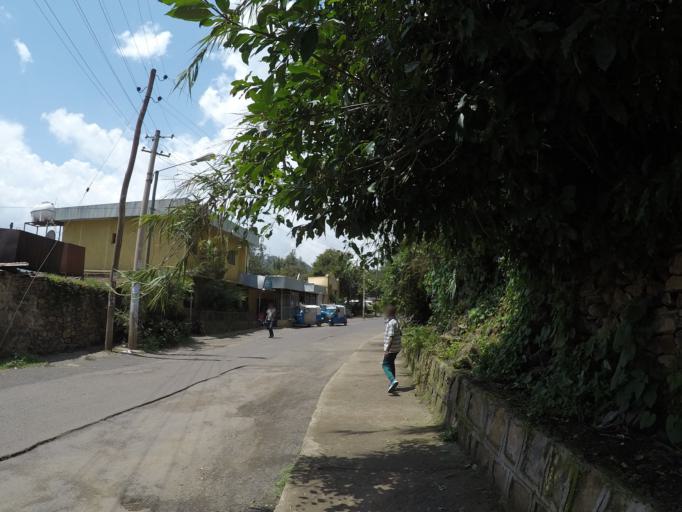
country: ET
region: Amhara
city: Gondar
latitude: 12.6104
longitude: 37.4706
